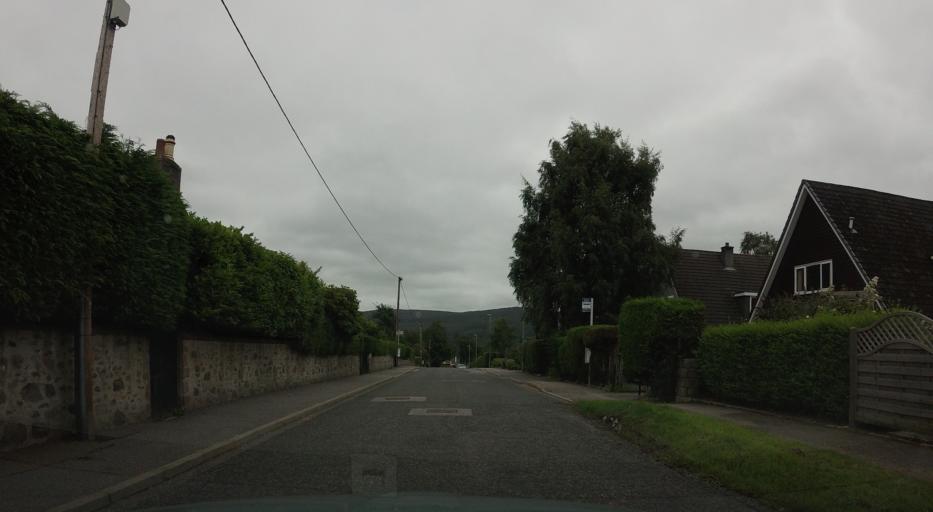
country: GB
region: Scotland
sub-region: Aberdeenshire
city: Banchory
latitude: 57.0553
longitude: -2.4971
